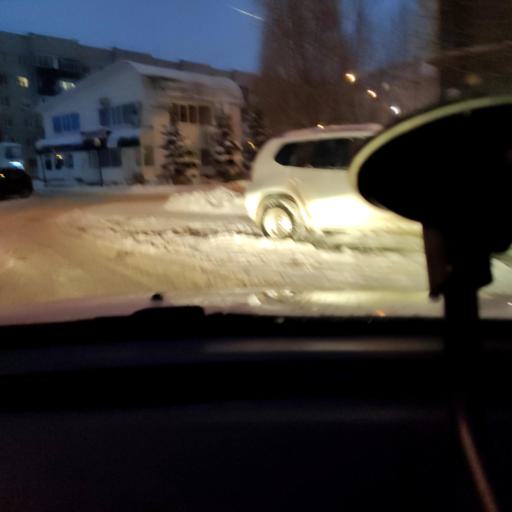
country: RU
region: Samara
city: Rozhdestveno
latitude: 53.1413
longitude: 50.0462
